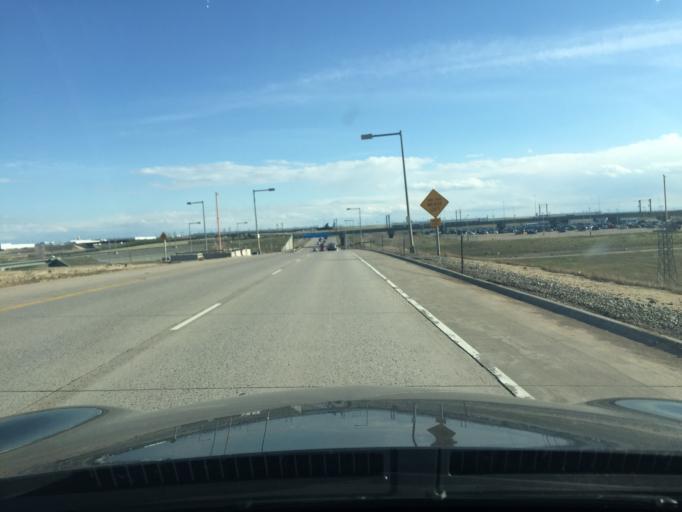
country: US
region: Colorado
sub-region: Weld County
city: Lochbuie
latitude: 39.8415
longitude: -104.6764
